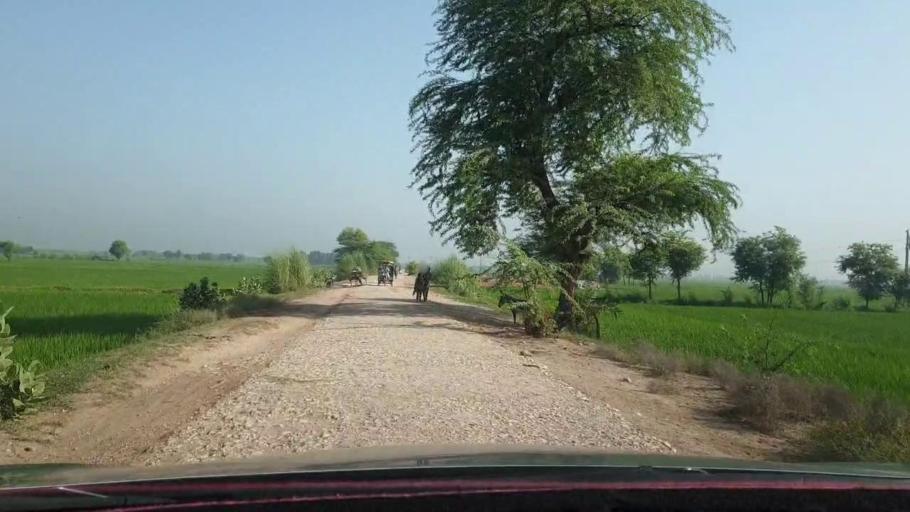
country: PK
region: Sindh
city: Nasirabad
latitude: 27.4347
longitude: 67.9204
